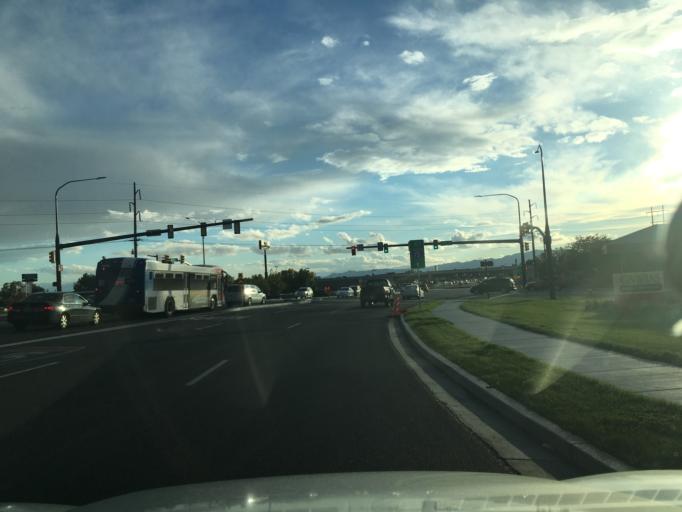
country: US
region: Utah
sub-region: Davis County
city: Layton
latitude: 41.0757
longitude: -111.9739
